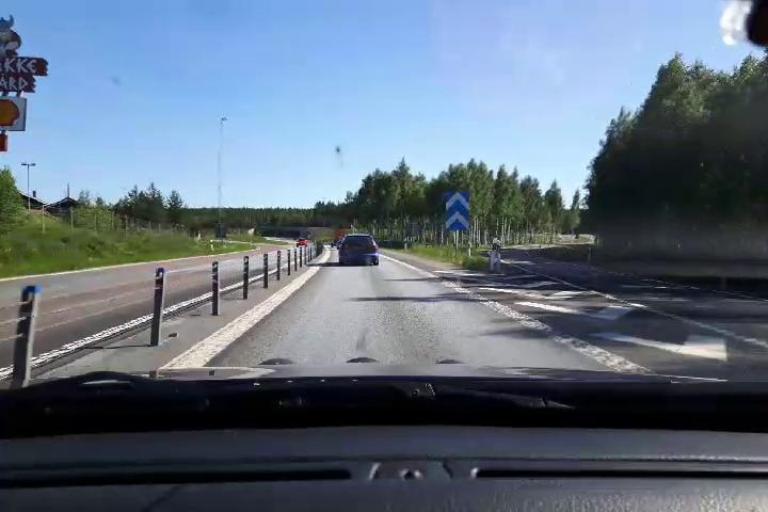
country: SE
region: Gaevleborg
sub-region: Gavle Kommun
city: Norrsundet
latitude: 60.9048
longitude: 17.0155
